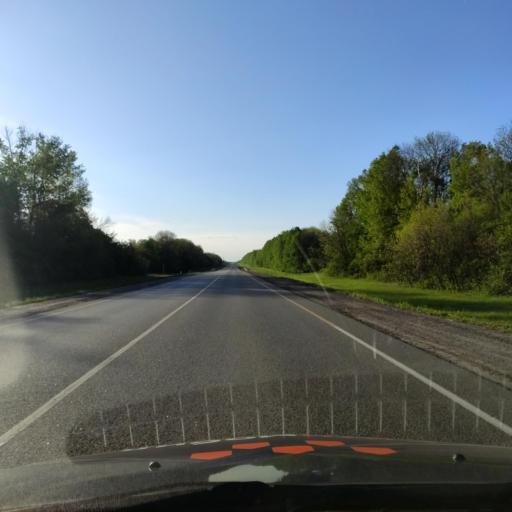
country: RU
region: Lipetsk
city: Yelets
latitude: 52.5730
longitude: 38.6550
